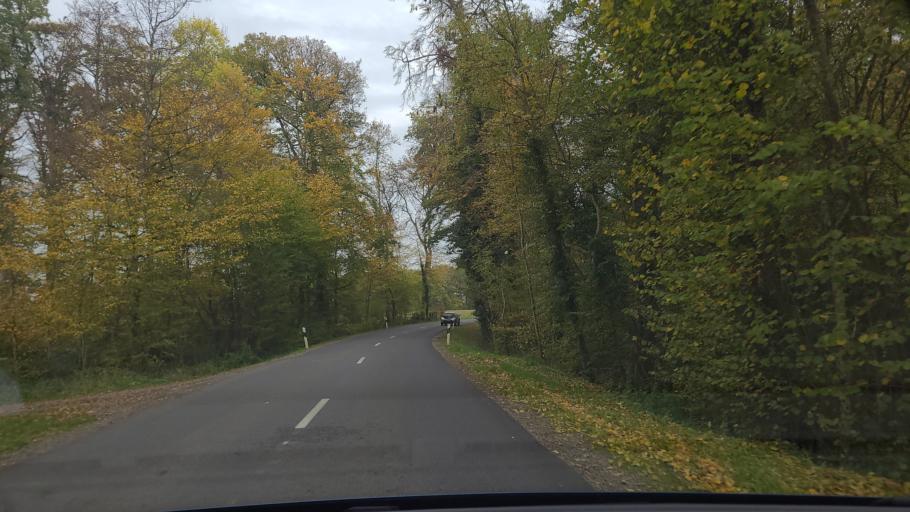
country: LU
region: Luxembourg
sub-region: Canton de Capellen
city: Dippach
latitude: 49.6011
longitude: 5.9906
